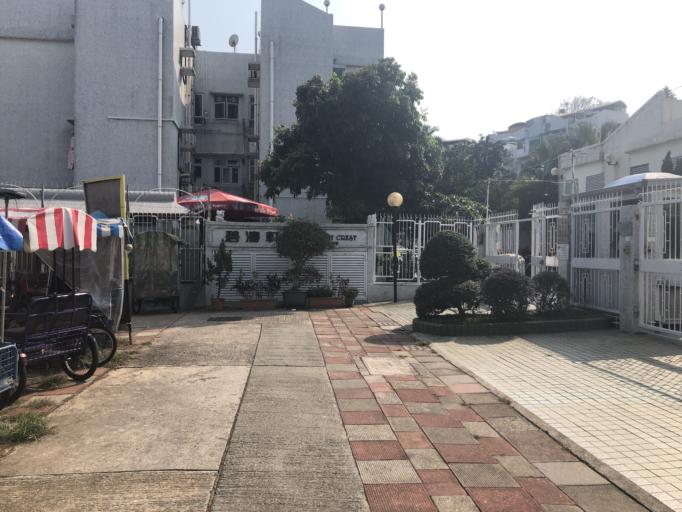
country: HK
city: Yung Shue Wan
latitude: 22.2047
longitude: 114.0243
